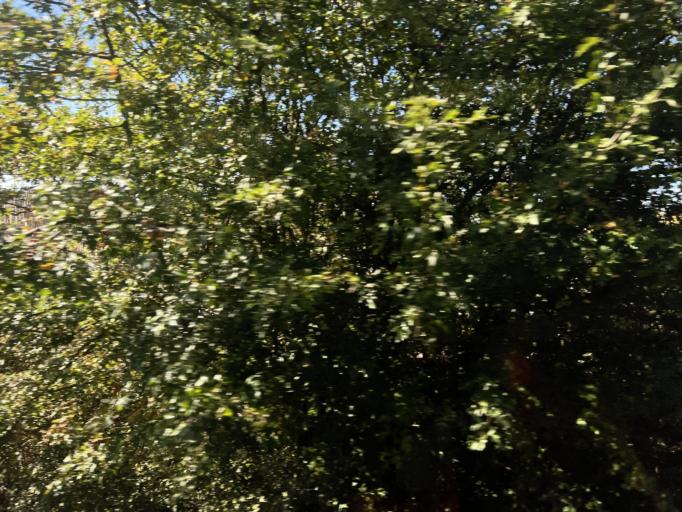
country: GB
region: England
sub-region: Lincolnshire
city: Heckington
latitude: 52.9808
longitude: -0.3130
